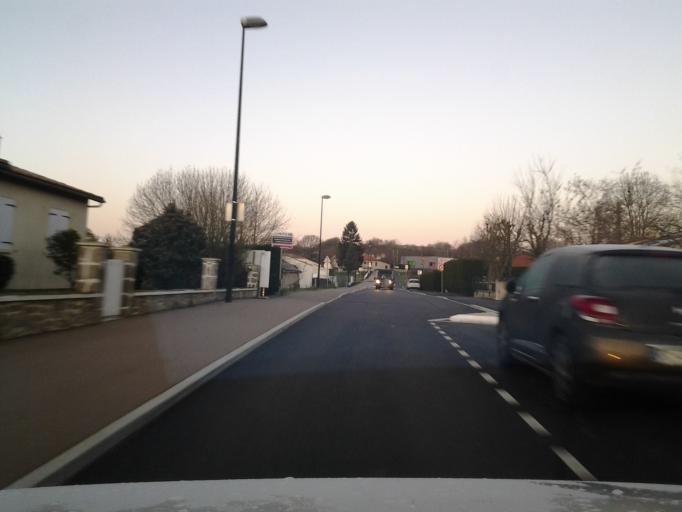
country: FR
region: Pays de la Loire
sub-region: Departement de la Vendee
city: Les Epesses
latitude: 46.8819
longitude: -0.9068
